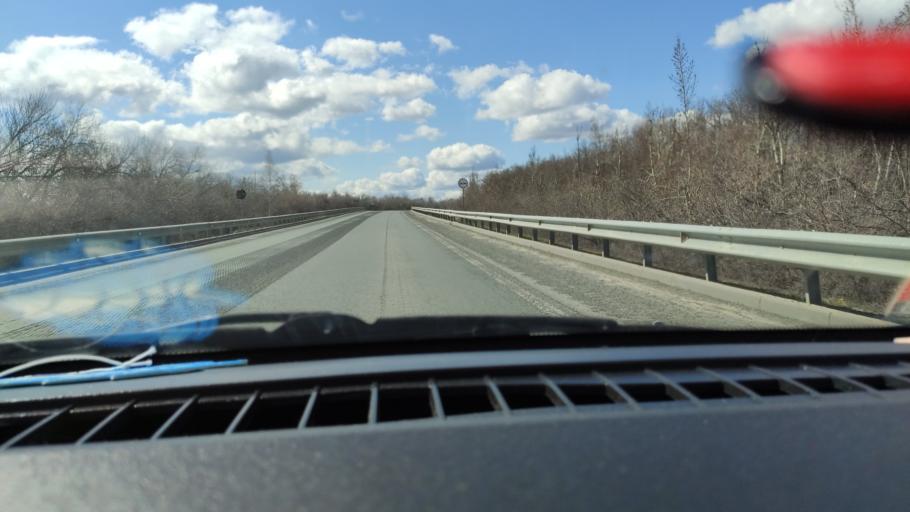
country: RU
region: Saratov
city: Dukhovnitskoye
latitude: 52.6229
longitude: 48.1757
